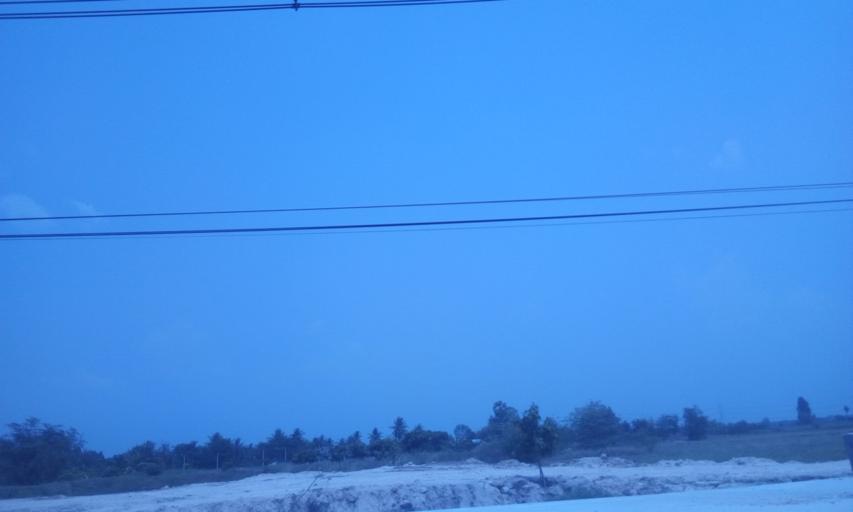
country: TH
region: Chon Buri
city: Phanat Nikhom
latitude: 13.4164
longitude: 101.1878
